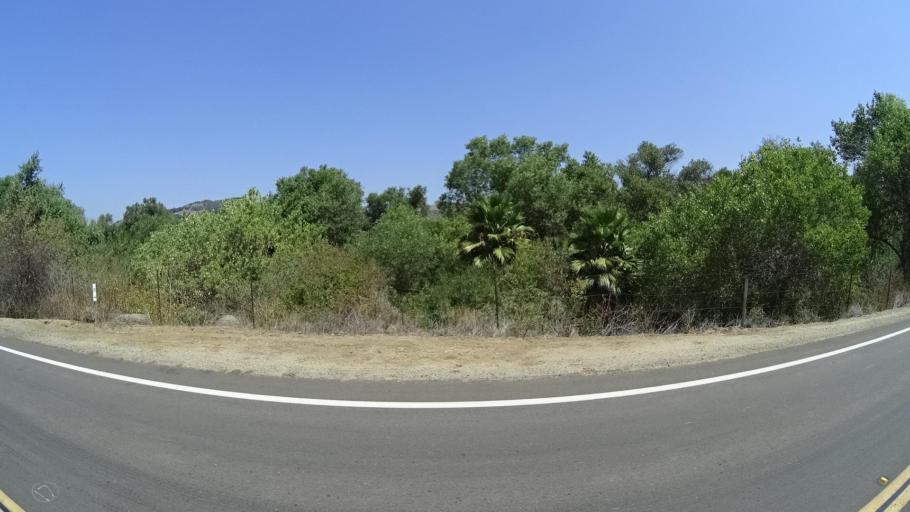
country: US
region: California
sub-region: San Diego County
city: Bonsall
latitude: 33.2708
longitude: -117.1732
